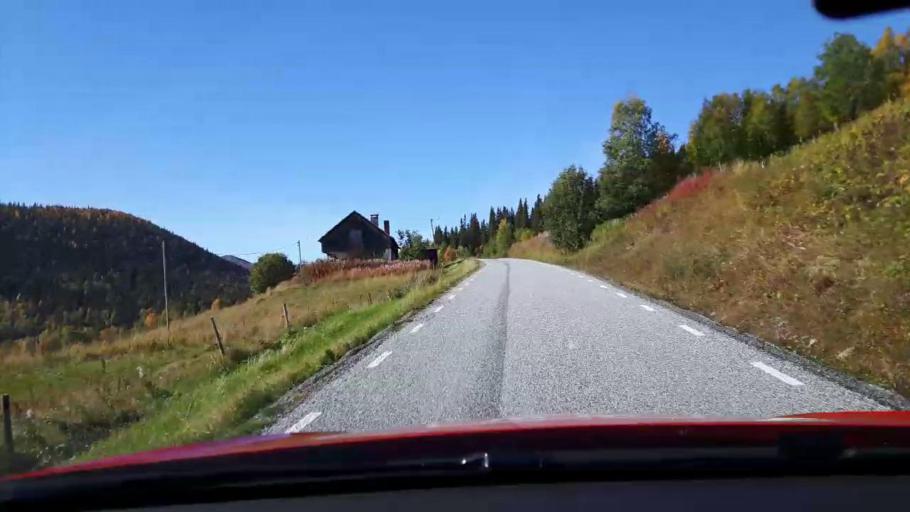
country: NO
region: Nord-Trondelag
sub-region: Royrvik
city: Royrvik
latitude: 64.8767
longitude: 14.2300
